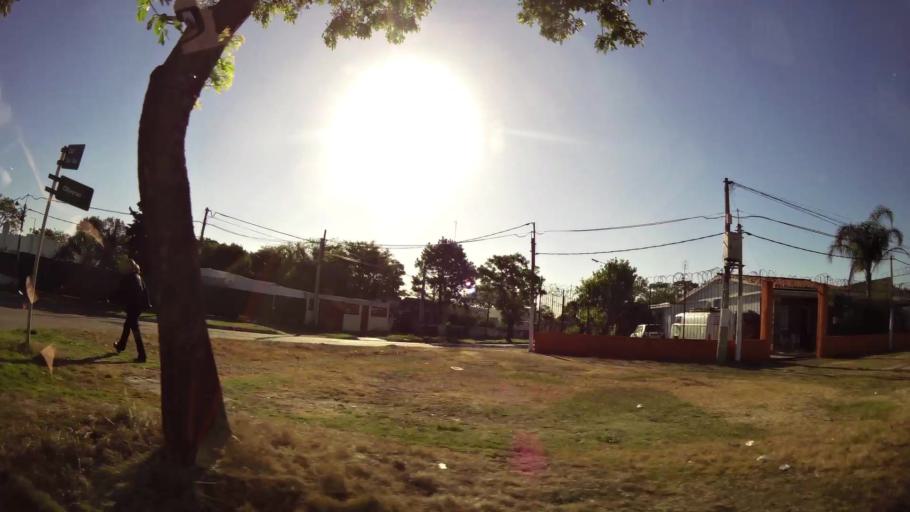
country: UY
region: Montevideo
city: Montevideo
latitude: -34.8372
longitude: -56.2011
